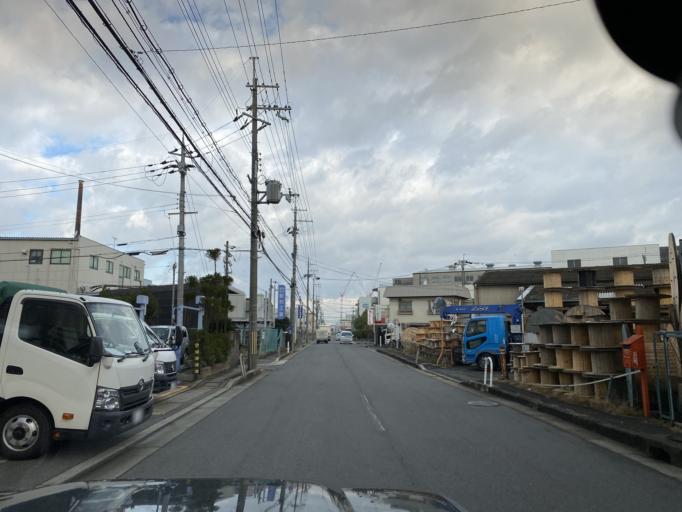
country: JP
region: Kyoto
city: Yawata
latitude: 34.8793
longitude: 135.7454
